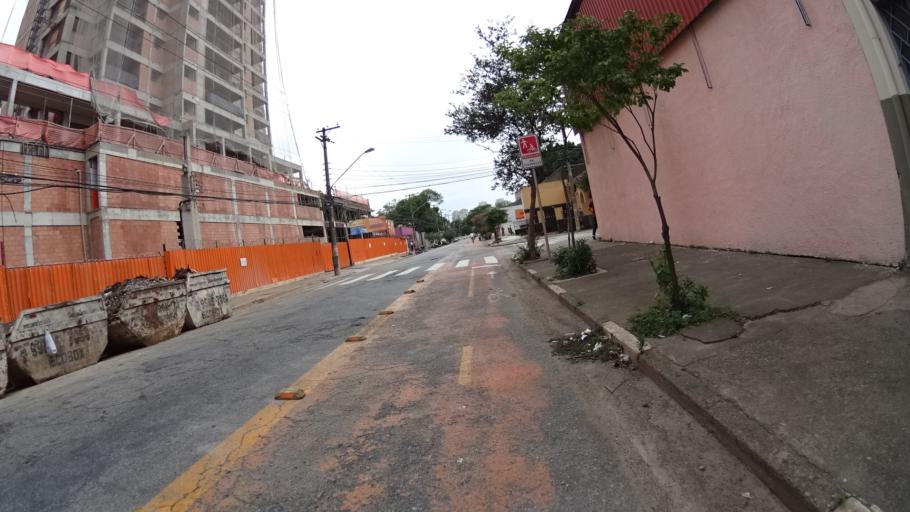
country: BR
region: Sao Paulo
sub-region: Sao Paulo
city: Sao Paulo
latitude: -23.5250
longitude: -46.6553
